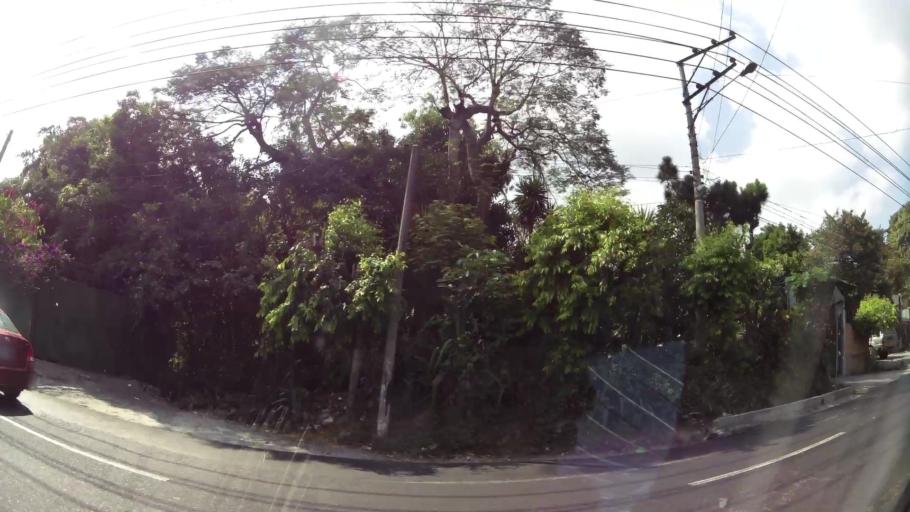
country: SV
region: San Salvador
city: Delgado
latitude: 13.7078
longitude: -89.1711
